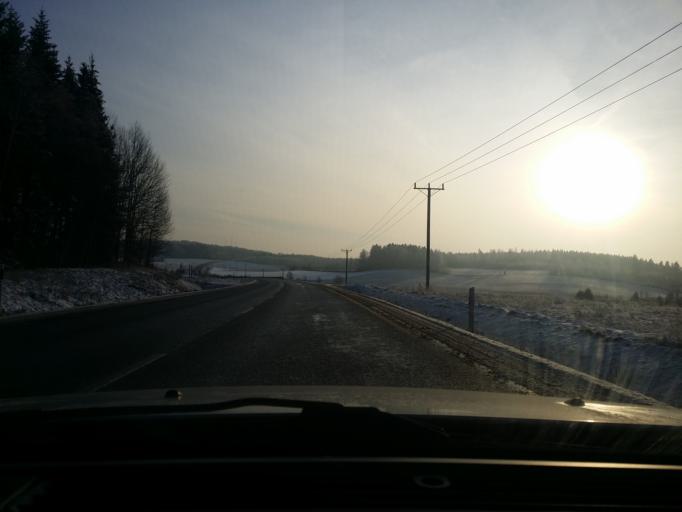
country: SE
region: OErebro
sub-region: Lindesbergs Kommun
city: Lindesberg
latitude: 59.5906
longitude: 15.1866
